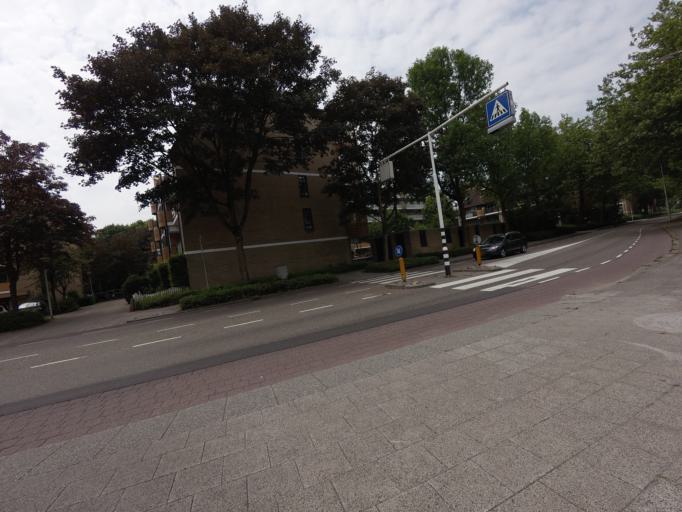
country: NL
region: South Holland
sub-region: Gemeente Gouda
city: Bloemendaal
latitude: 52.0253
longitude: 4.6907
